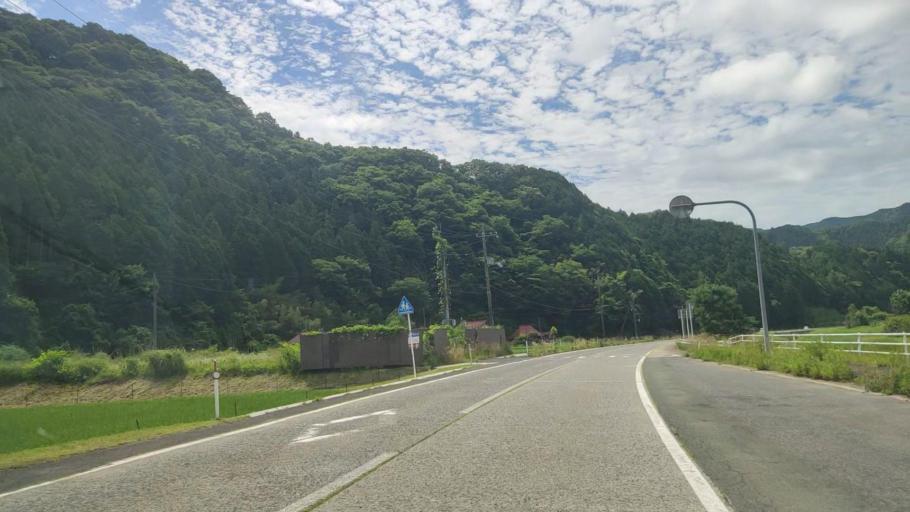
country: JP
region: Okayama
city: Niimi
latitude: 35.1704
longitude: 133.5792
